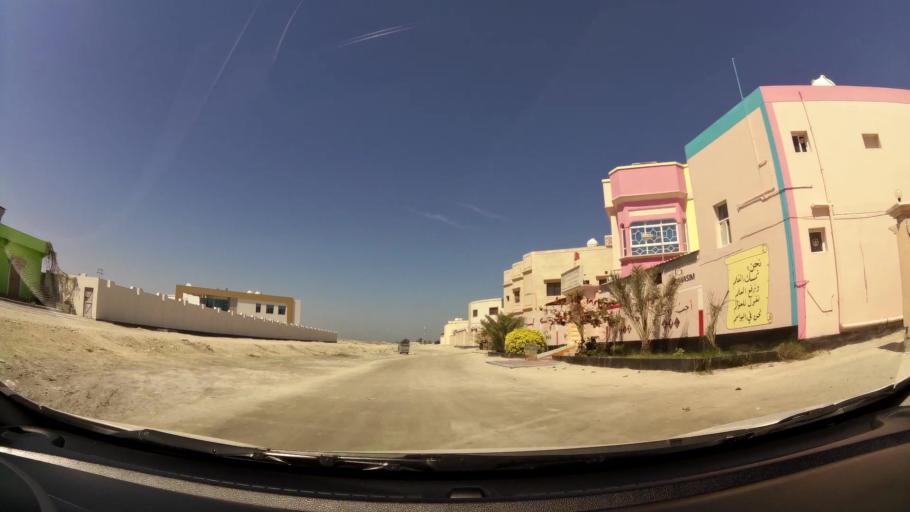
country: BH
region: Muharraq
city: Al Muharraq
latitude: 26.2870
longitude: 50.6264
